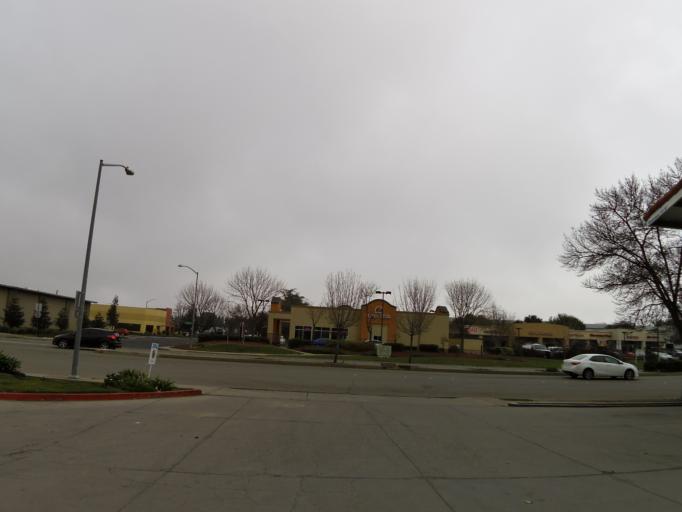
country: US
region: California
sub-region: Alameda County
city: Livermore
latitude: 37.7059
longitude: -121.7229
